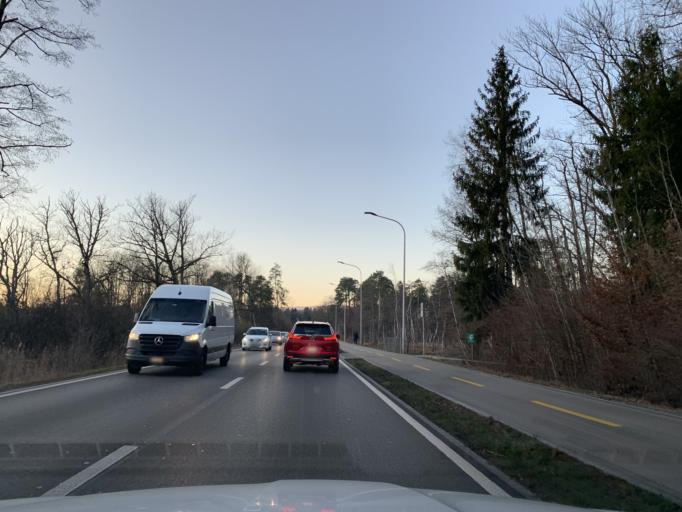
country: CH
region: Zurich
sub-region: Bezirk Zuerich
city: Zuerich (Kreis 10) / Ruetihof
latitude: 47.4299
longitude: 8.4870
